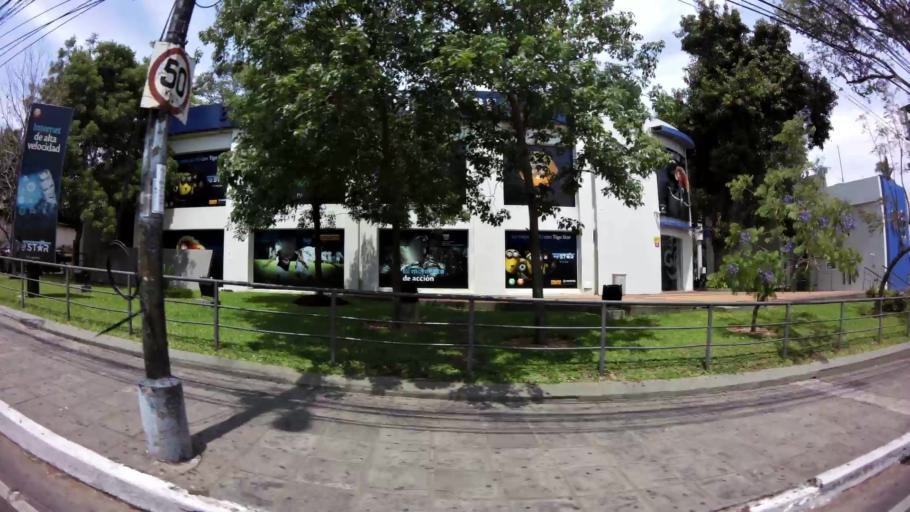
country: PY
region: Central
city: Lambare
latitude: -25.2957
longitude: -57.5765
